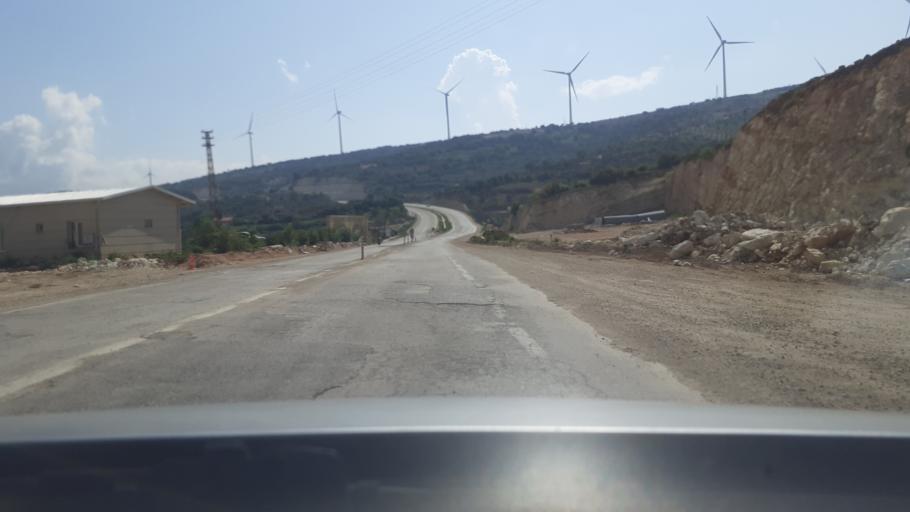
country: TR
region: Hatay
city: Senkoy
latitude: 36.0528
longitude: 36.1446
